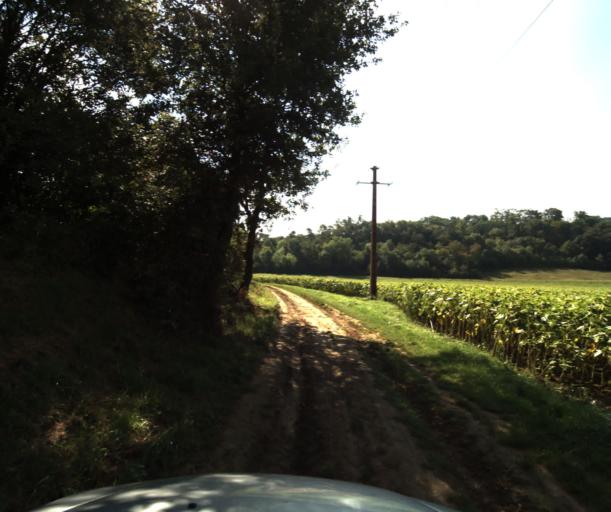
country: FR
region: Midi-Pyrenees
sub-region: Departement de la Haute-Garonne
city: Portet-sur-Garonne
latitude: 43.5180
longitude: 1.4227
